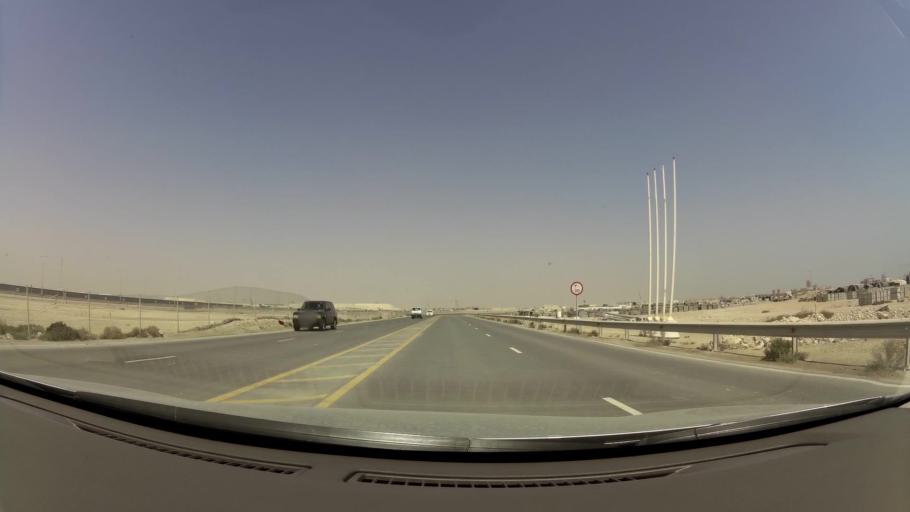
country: QA
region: Baladiyat Umm Salal
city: Umm Salal Muhammad
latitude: 25.3996
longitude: 51.4954
